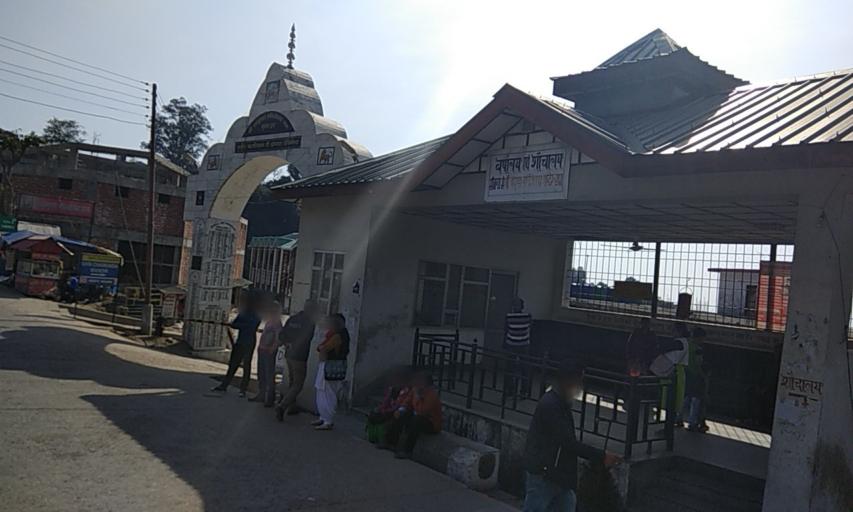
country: IN
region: Himachal Pradesh
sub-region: Kangra
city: Dharmsala
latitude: 32.1494
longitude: 76.4201
